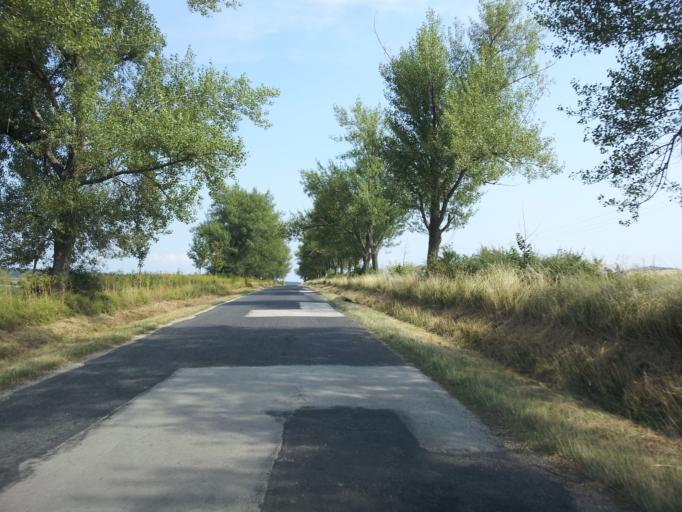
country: HU
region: Veszprem
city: Nemesvamos
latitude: 47.0130
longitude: 17.8150
